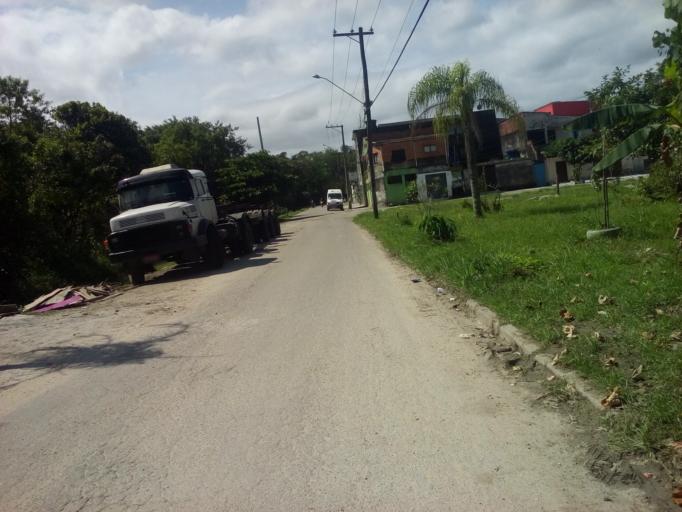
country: BR
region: Sao Paulo
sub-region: Guaruja
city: Guaruja
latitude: -23.9647
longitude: -46.2599
